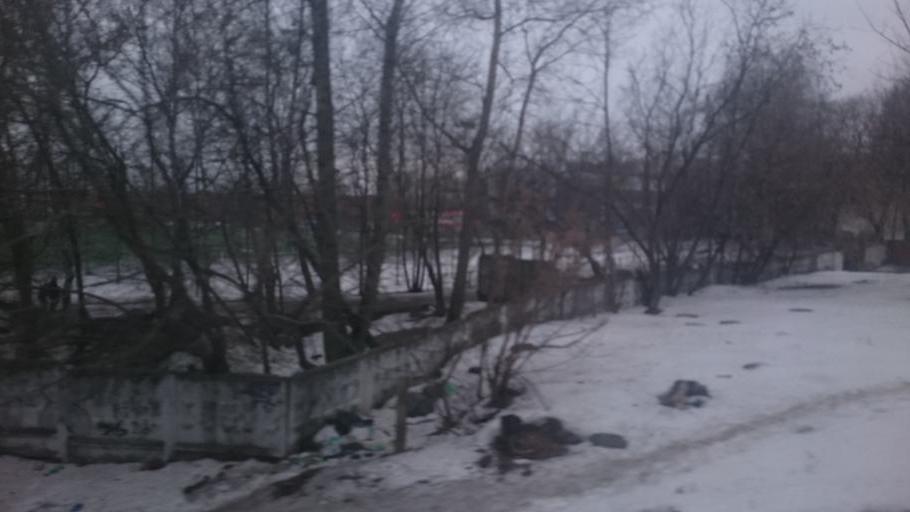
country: RU
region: Moscow
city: Pokrovskoye-Streshnevo
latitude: 55.8233
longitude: 37.4478
